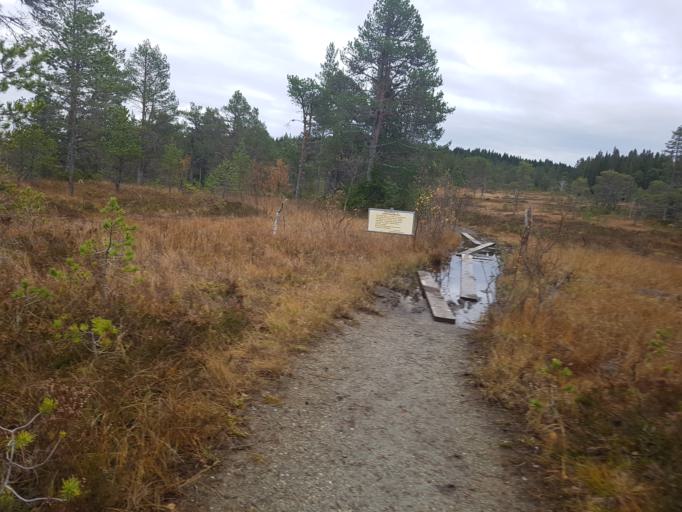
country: NO
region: Sor-Trondelag
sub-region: Melhus
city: Melhus
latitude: 63.3843
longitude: 10.2453
